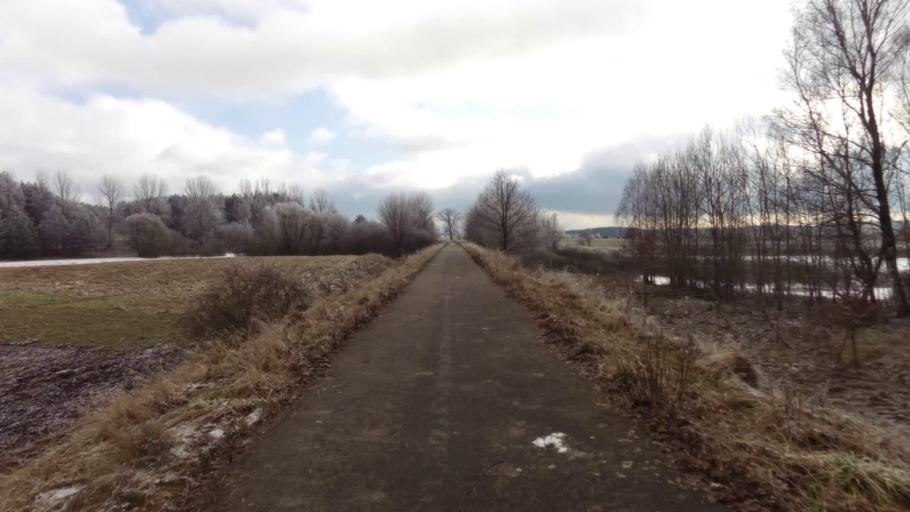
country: PL
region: West Pomeranian Voivodeship
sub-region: Powiat drawski
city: Zlocieniec
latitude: 53.6396
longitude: 16.0457
